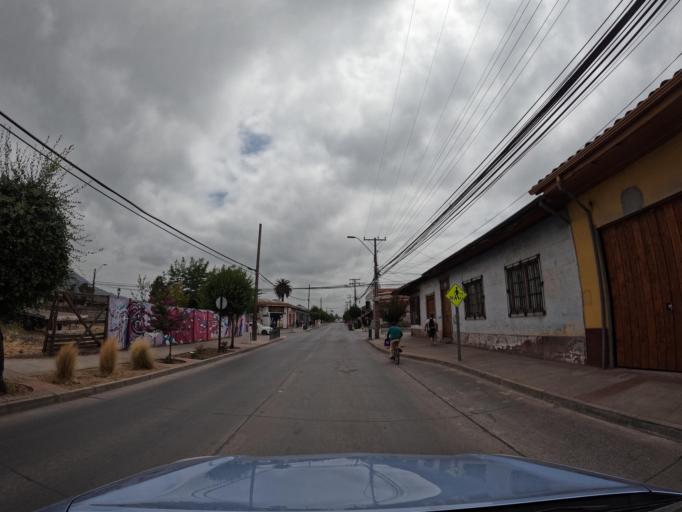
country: CL
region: O'Higgins
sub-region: Provincia de Colchagua
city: Chimbarongo
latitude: -34.7110
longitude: -71.0454
